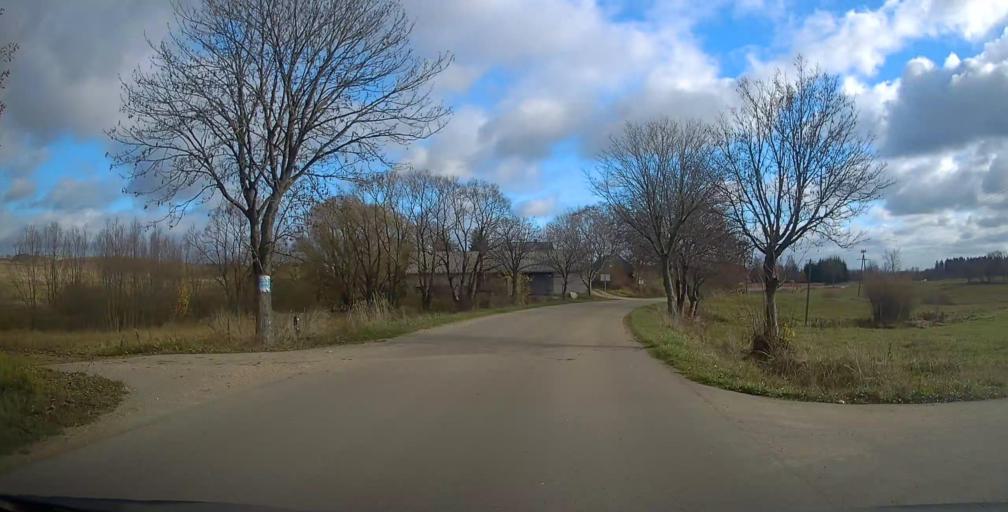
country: PL
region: Podlasie
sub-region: Suwalki
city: Suwalki
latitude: 54.3164
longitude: 22.8738
